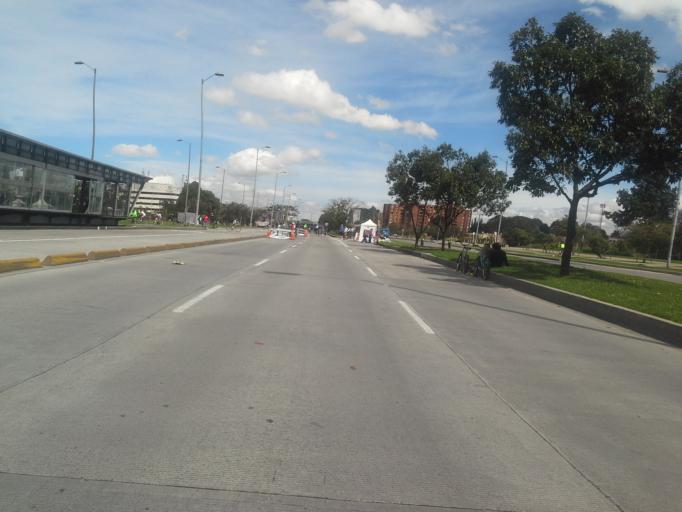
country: CO
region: Bogota D.C.
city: Bogota
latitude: 4.6471
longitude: -74.0990
